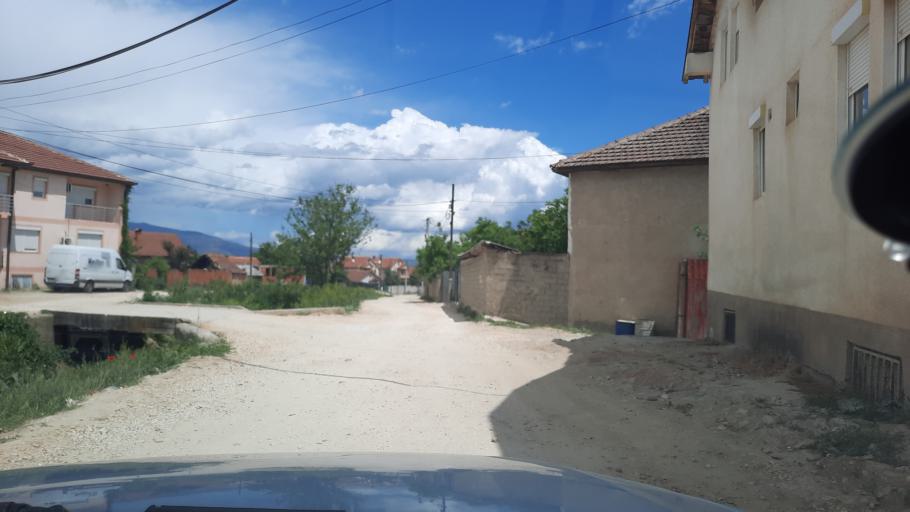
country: MK
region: Studenicani
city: Studenichani
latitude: 41.9221
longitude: 21.5359
